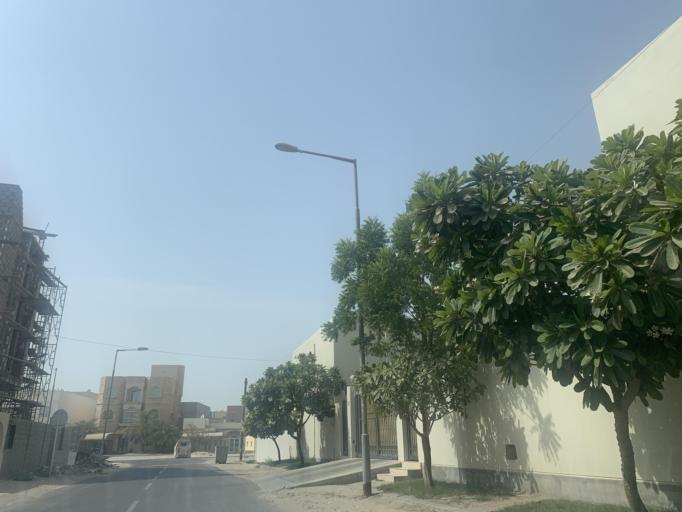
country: BH
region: Manama
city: Jidd Hafs
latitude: 26.2093
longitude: 50.4673
